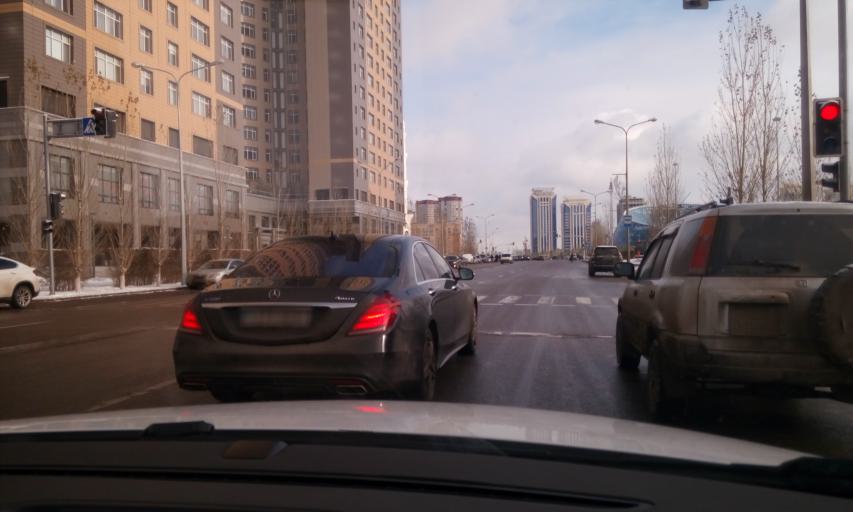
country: KZ
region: Astana Qalasy
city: Astana
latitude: 51.1254
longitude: 71.4664
